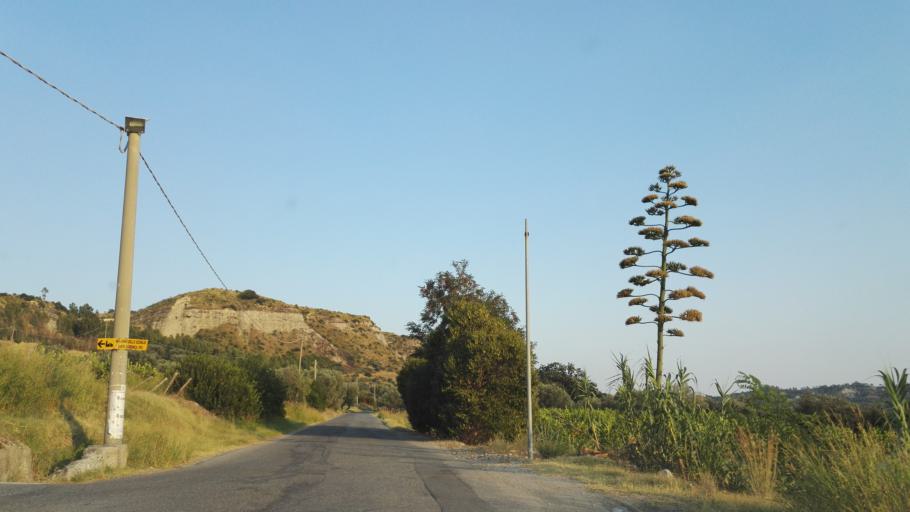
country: IT
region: Calabria
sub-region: Provincia di Reggio Calabria
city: Caulonia
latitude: 38.3936
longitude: 16.4285
